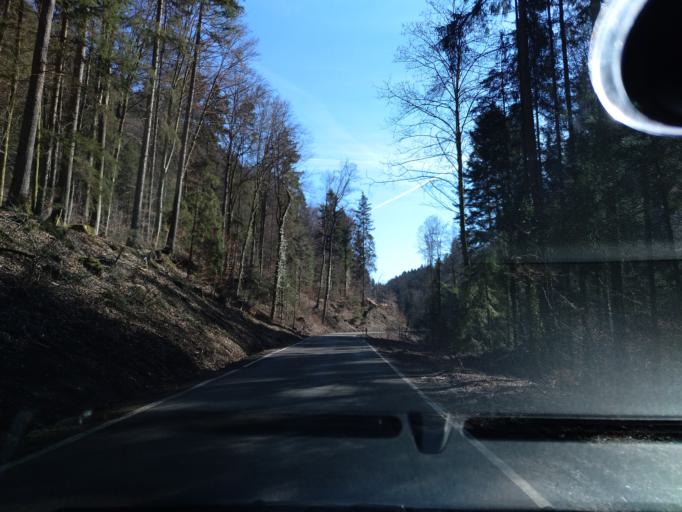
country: DE
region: Baden-Wuerttemberg
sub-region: Regierungsbezirk Stuttgart
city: Mainhardt
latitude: 49.0930
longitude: 9.5445
